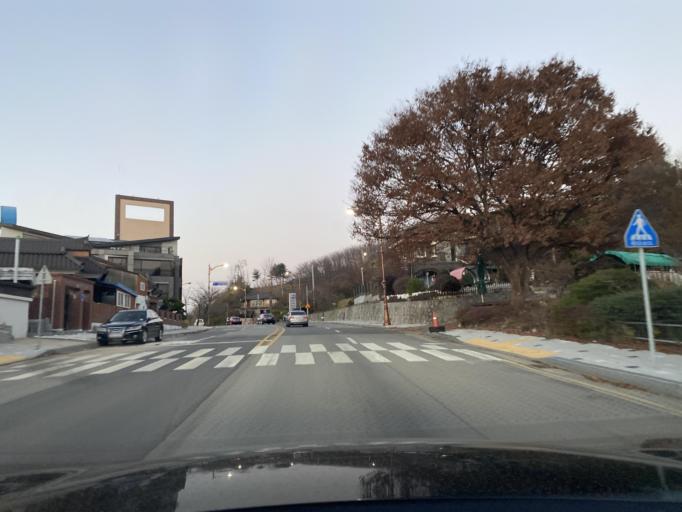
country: KR
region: Chungcheongnam-do
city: Yesan
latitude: 36.6834
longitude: 126.8355
